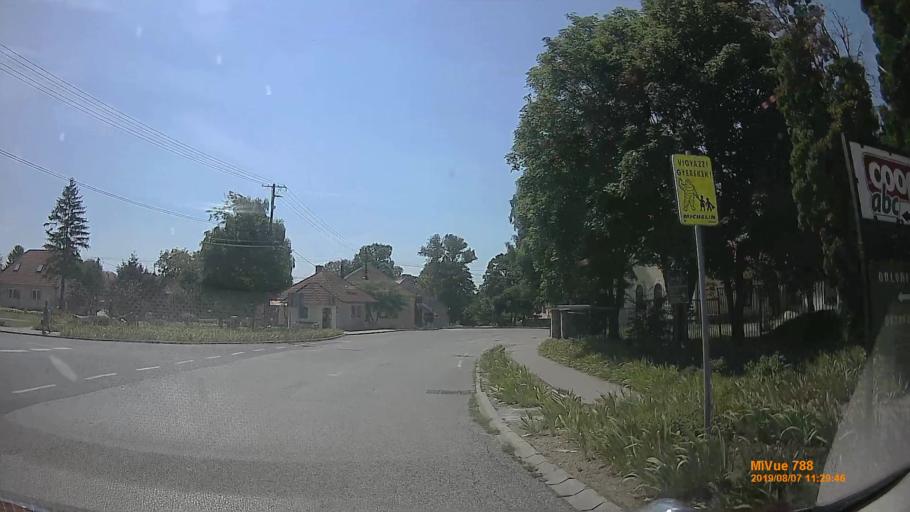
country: HU
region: Veszprem
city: Tapolca
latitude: 46.9151
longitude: 17.4578
